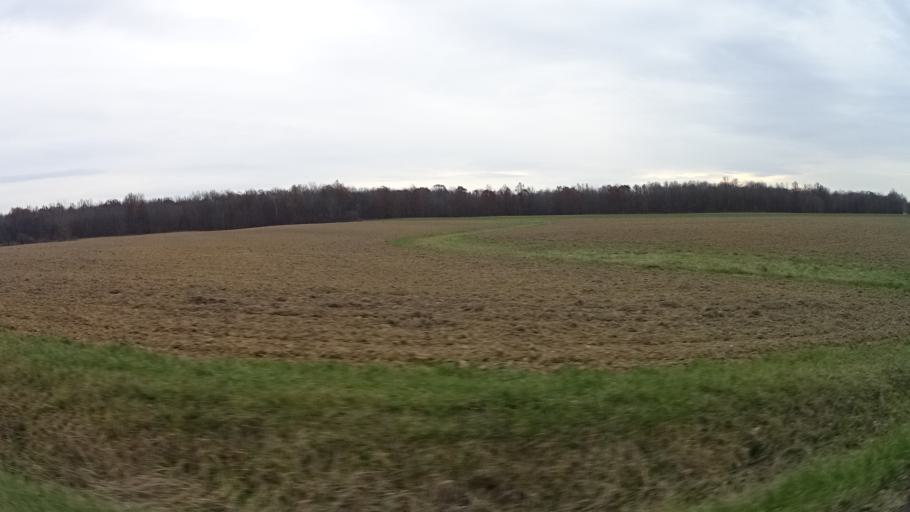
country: US
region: Ohio
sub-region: Lorain County
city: Lagrange
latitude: 41.2024
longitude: -82.0778
